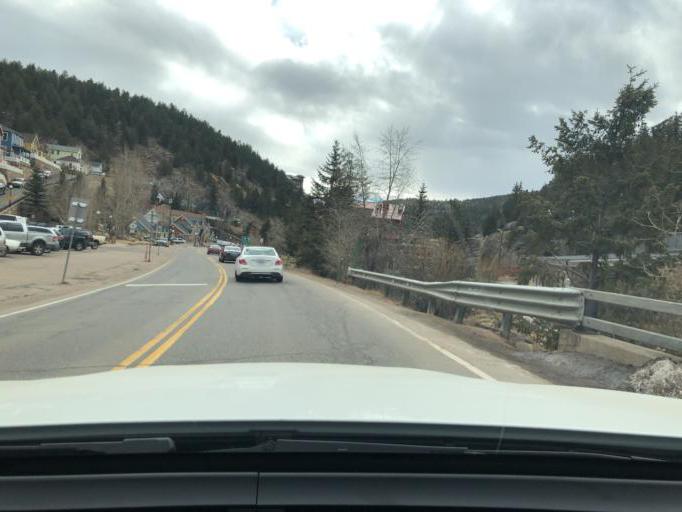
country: US
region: Colorado
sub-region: Gilpin County
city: Central City
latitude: 39.8044
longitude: -105.4976
